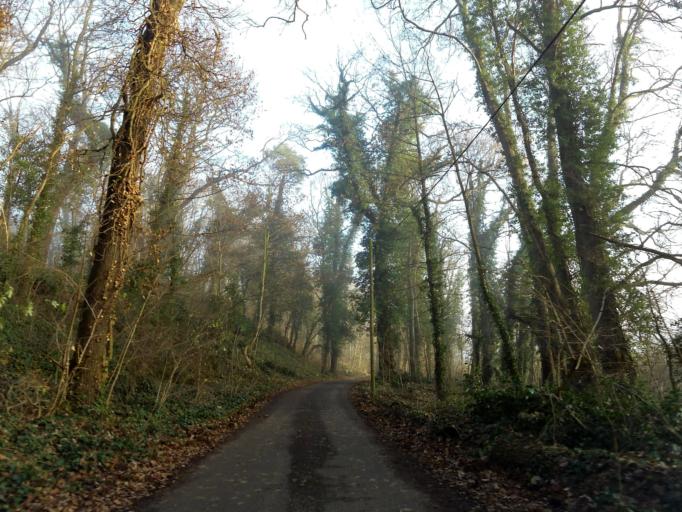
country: DE
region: Brandenburg
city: Michendorf
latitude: 52.3586
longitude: 12.9920
